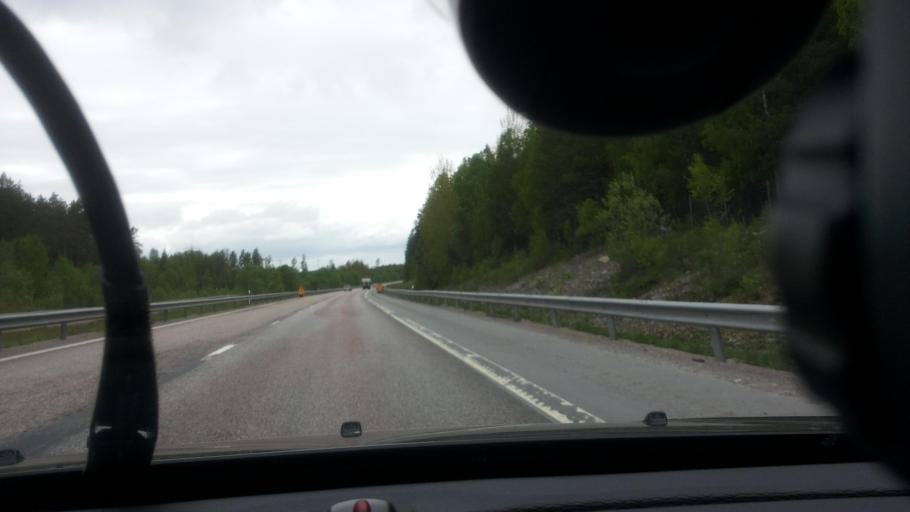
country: SE
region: Uppsala
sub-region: Alvkarleby Kommun
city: AElvkarleby
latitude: 60.4724
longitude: 17.3900
